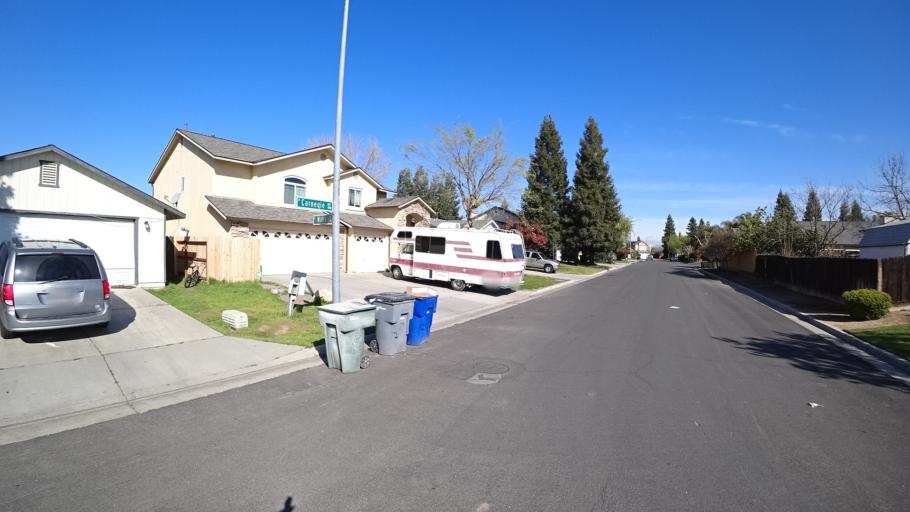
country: US
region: California
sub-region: Fresno County
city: West Park
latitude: 36.7955
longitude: -119.8935
